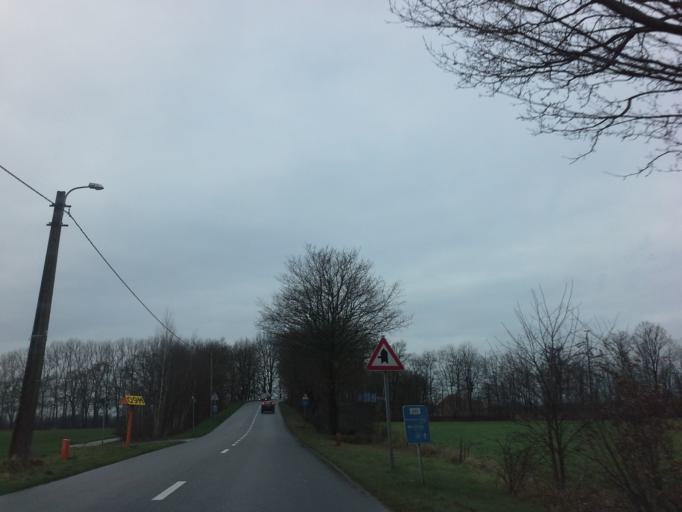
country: BE
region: Flanders
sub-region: Provincie Limburg
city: Leopoldsburg
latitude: 51.1541
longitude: 5.2548
